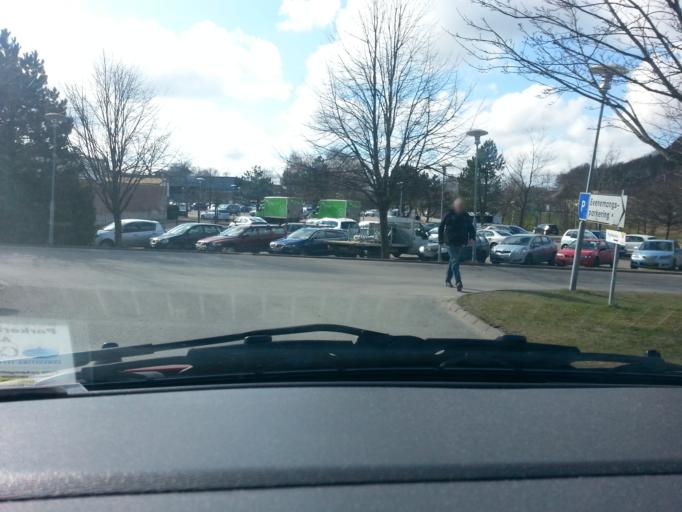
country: SE
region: Vaestra Goetaland
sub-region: Partille Kommun
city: Partille
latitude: 57.7410
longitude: 12.1091
